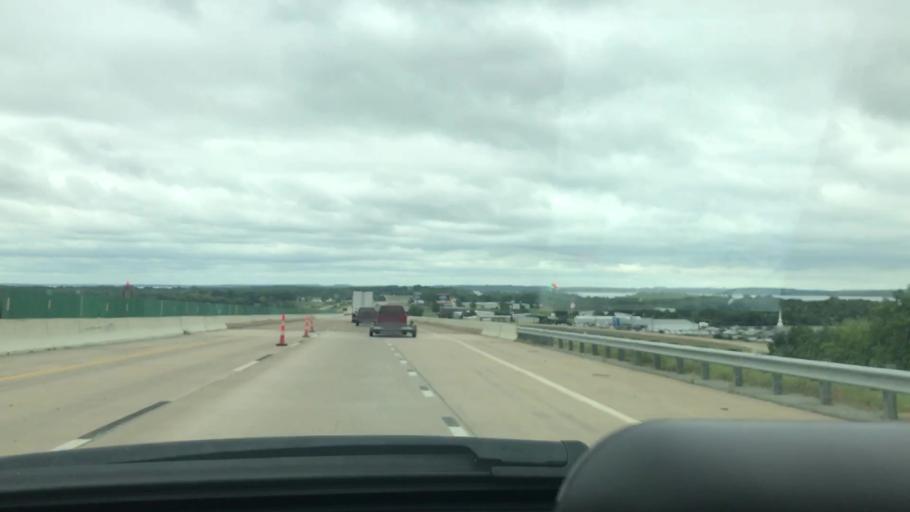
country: US
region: Oklahoma
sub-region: McIntosh County
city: Eufaula
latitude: 35.2920
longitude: -95.5931
